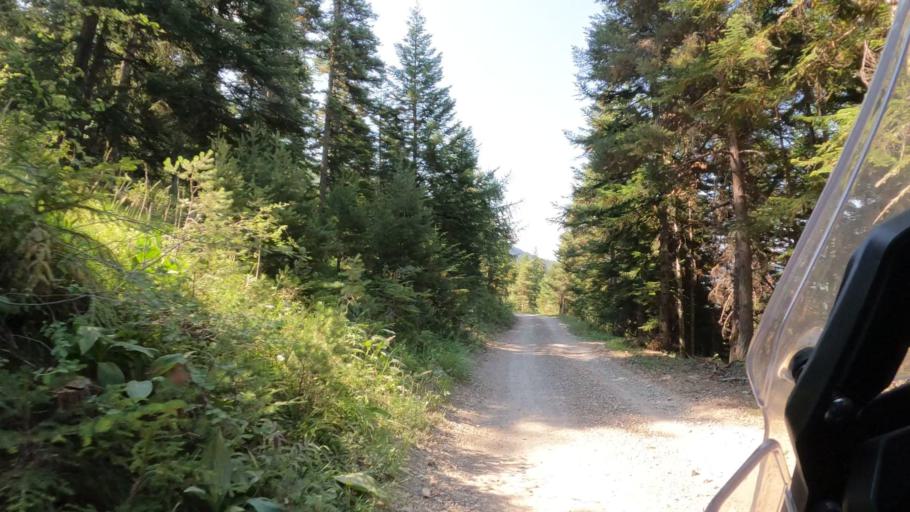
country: FR
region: Provence-Alpes-Cote d'Azur
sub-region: Departement des Hautes-Alpes
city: Embrun
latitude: 44.5966
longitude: 6.5630
